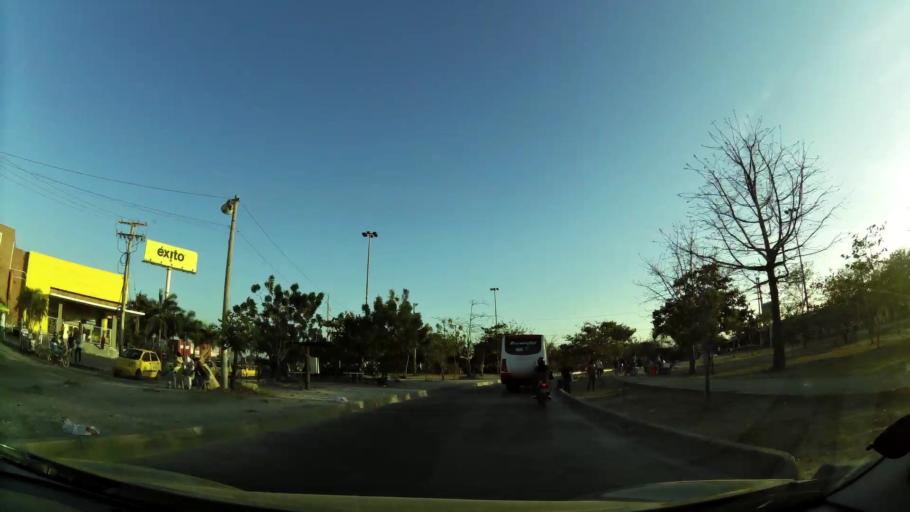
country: CO
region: Atlantico
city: Soledad
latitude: 10.9244
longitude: -74.7983
